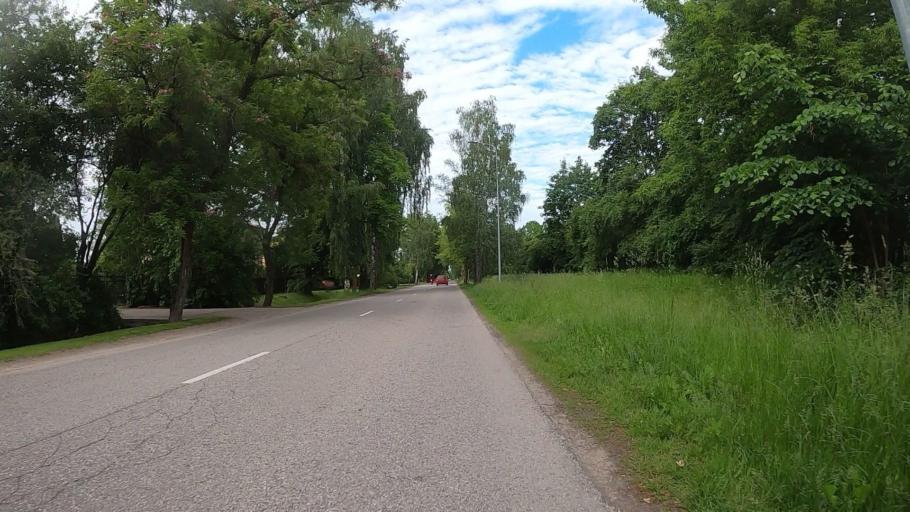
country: LV
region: Jelgava
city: Jelgava
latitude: 56.6629
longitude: 23.7439
